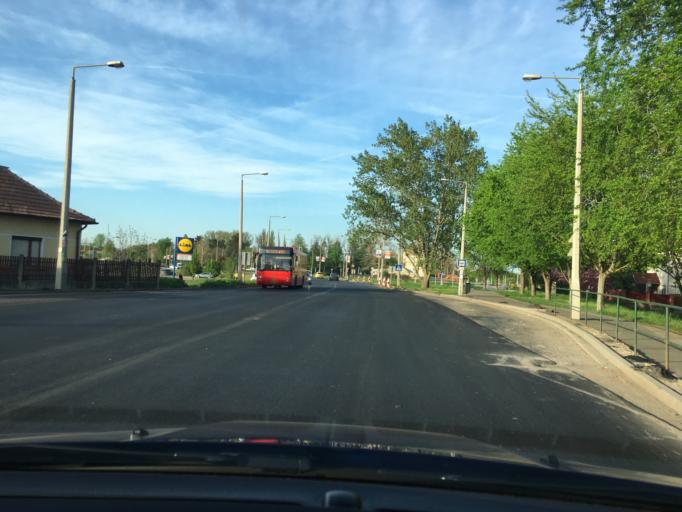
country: HU
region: Hajdu-Bihar
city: Berettyoujfalu
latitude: 47.2322
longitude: 21.5327
